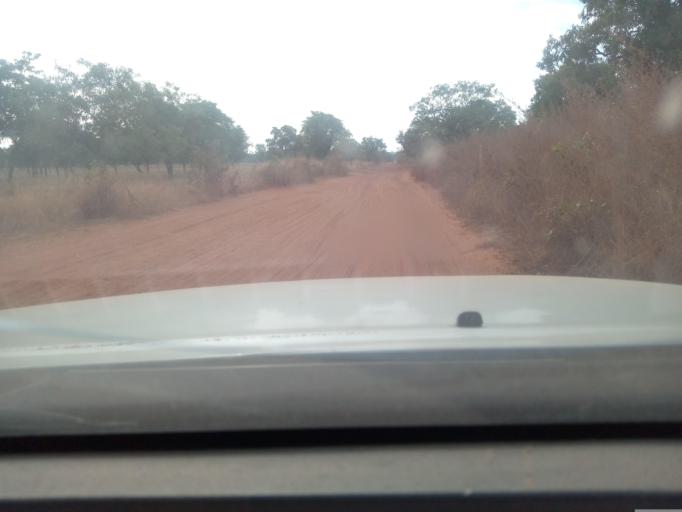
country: ML
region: Sikasso
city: Sikasso
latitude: 11.9482
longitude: -6.0843
